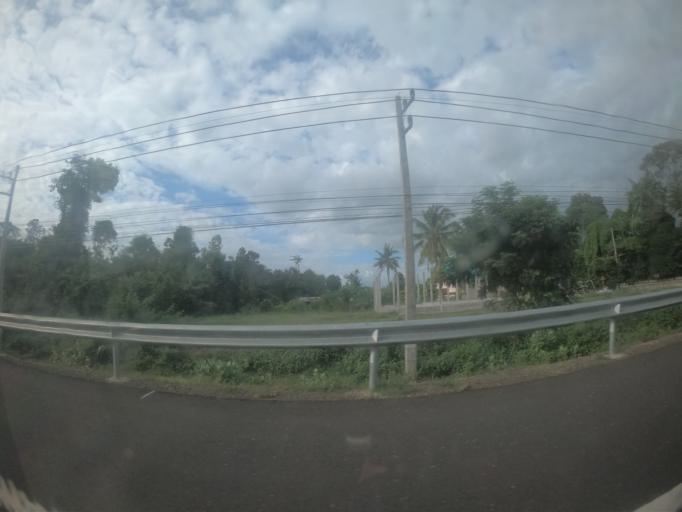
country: TH
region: Surin
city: Prasat
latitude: 14.5886
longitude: 103.4685
